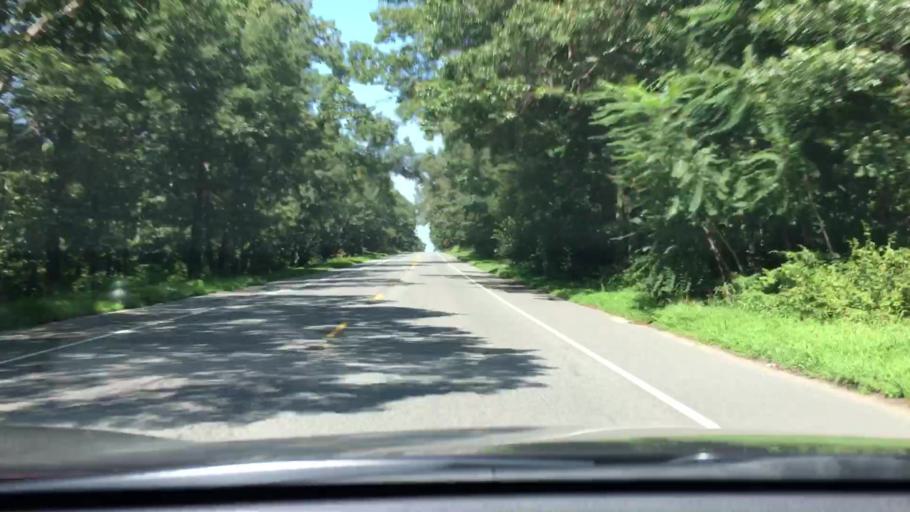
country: US
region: New Jersey
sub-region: Cumberland County
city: Laurel Lake
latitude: 39.3506
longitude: -75.0538
